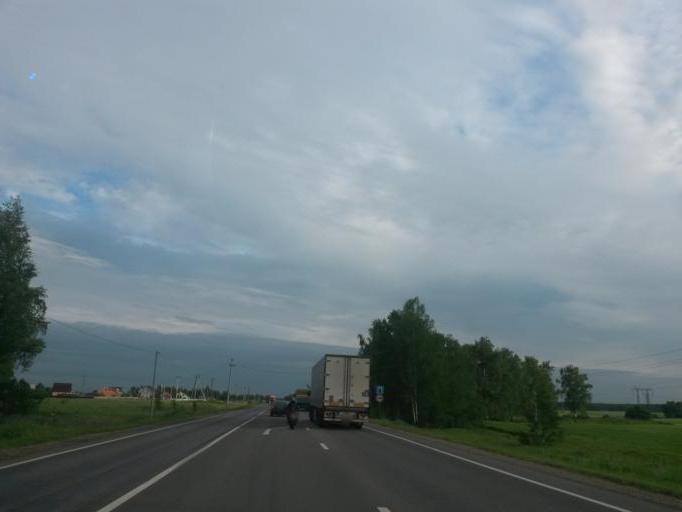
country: RU
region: Moskovskaya
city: Belyye Stolby
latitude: 55.2762
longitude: 37.8254
